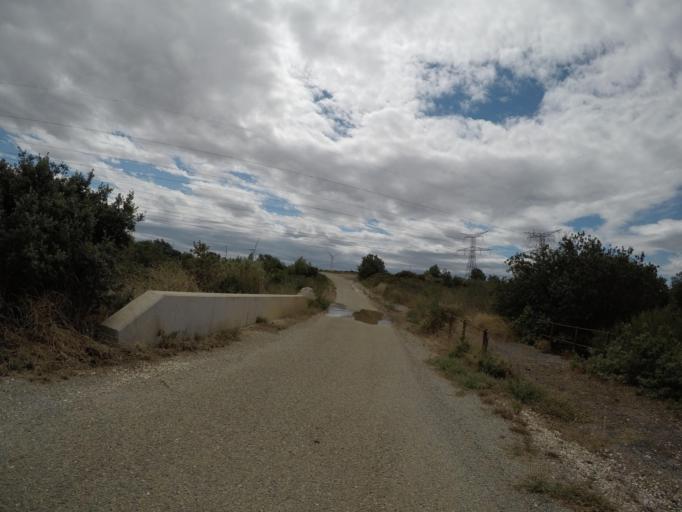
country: FR
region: Languedoc-Roussillon
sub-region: Departement des Pyrenees-Orientales
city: Corneilla-la-Riviere
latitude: 42.7212
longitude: 2.7456
